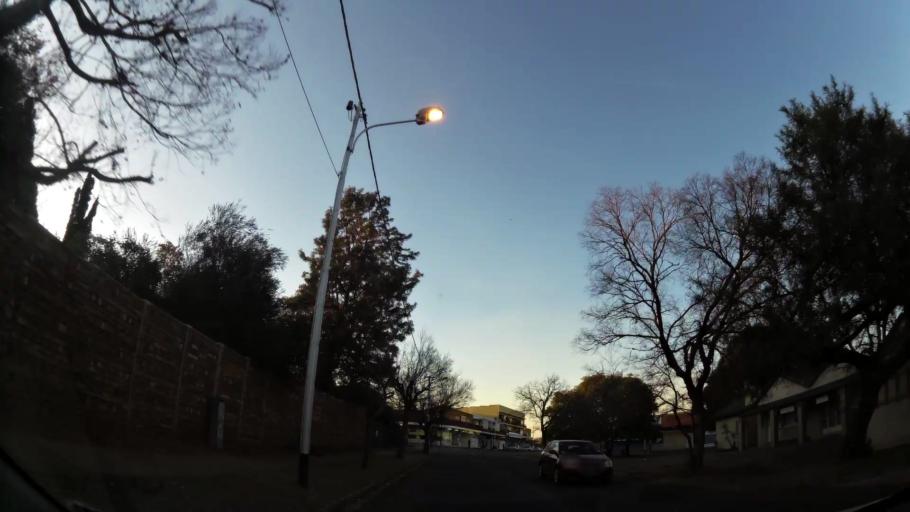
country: ZA
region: Gauteng
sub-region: City of Johannesburg Metropolitan Municipality
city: Roodepoort
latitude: -26.1570
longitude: 27.8941
